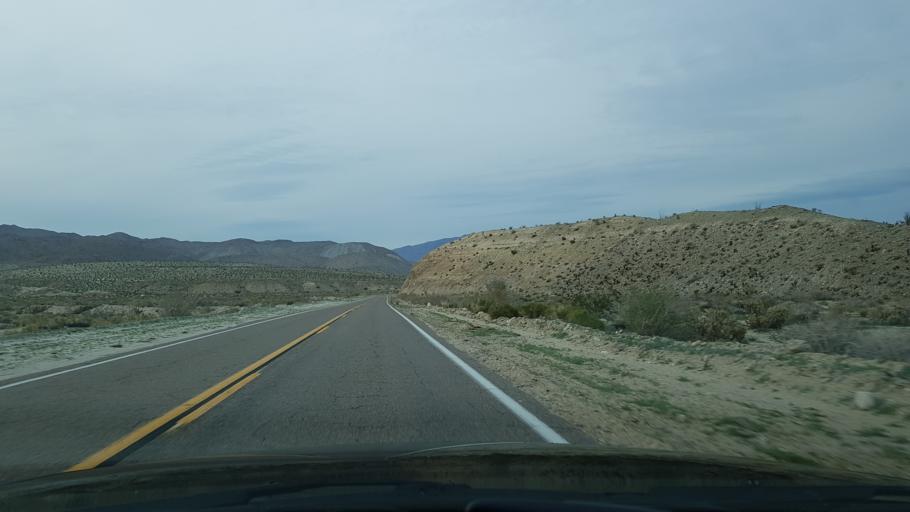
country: US
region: California
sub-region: San Diego County
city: Pine Valley
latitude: 32.8404
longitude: -116.1955
